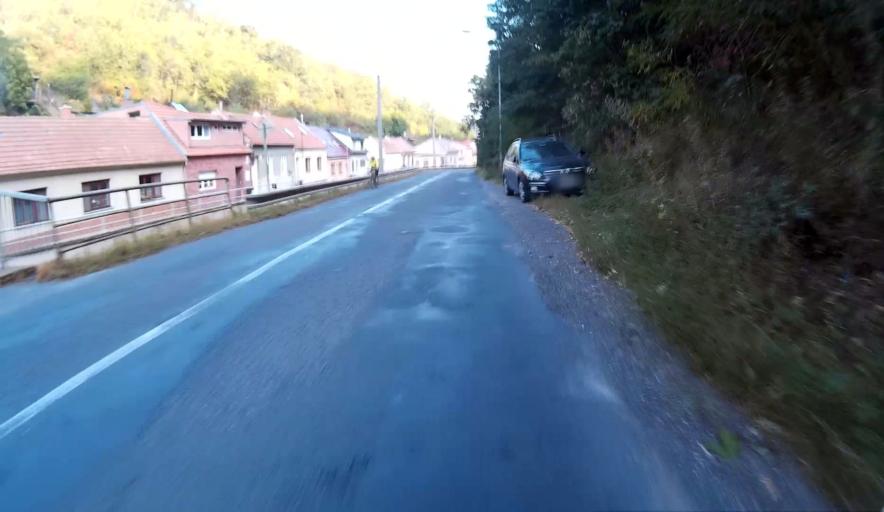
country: CZ
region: South Moravian
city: Podoli
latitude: 49.2057
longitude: 16.7049
